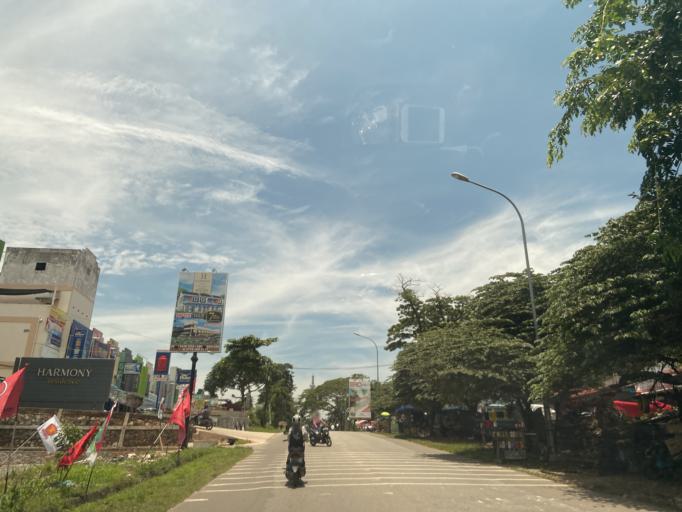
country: SG
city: Singapore
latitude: 1.1545
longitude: 104.0239
